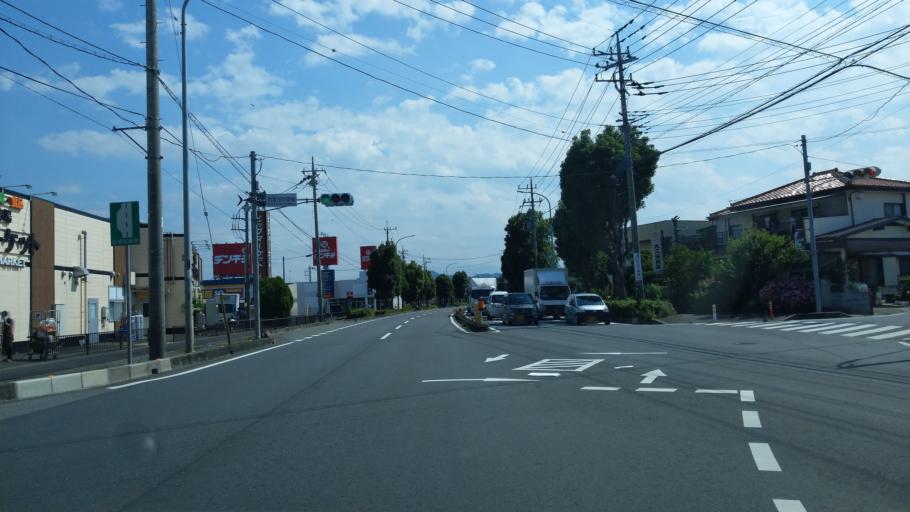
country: JP
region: Saitama
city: Honjo
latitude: 36.2306
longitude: 139.1686
